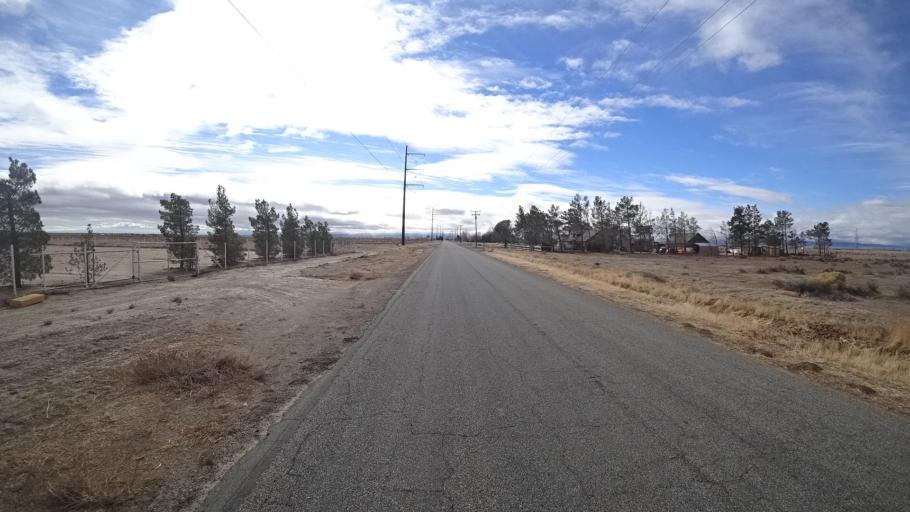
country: US
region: California
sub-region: Kern County
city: Rosamond
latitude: 34.8551
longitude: -118.3088
